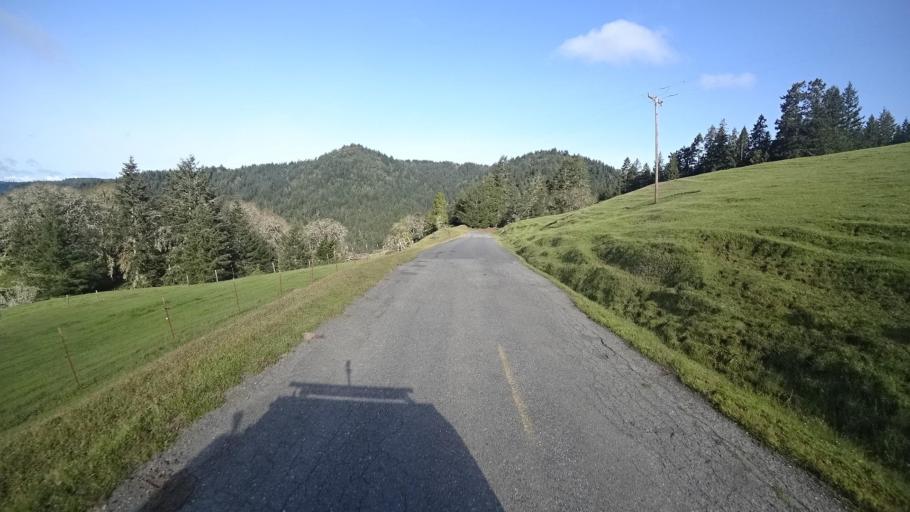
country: US
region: California
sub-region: Humboldt County
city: Bayside
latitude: 40.6907
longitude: -123.9390
